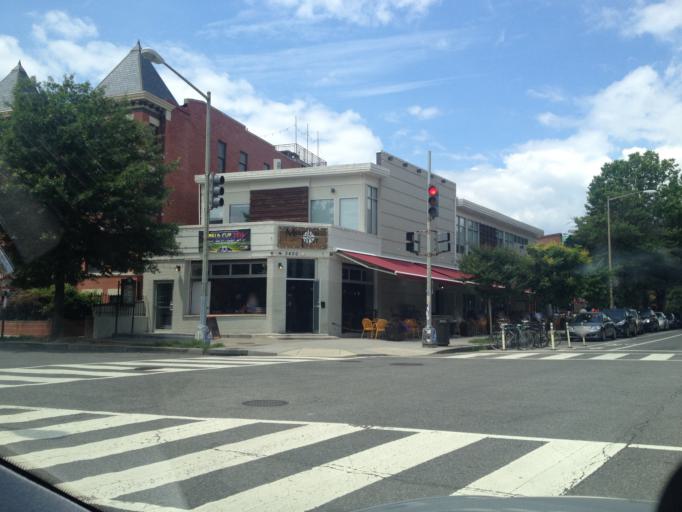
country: US
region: Washington, D.C.
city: Washington, D.C.
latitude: 38.9317
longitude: -77.0282
